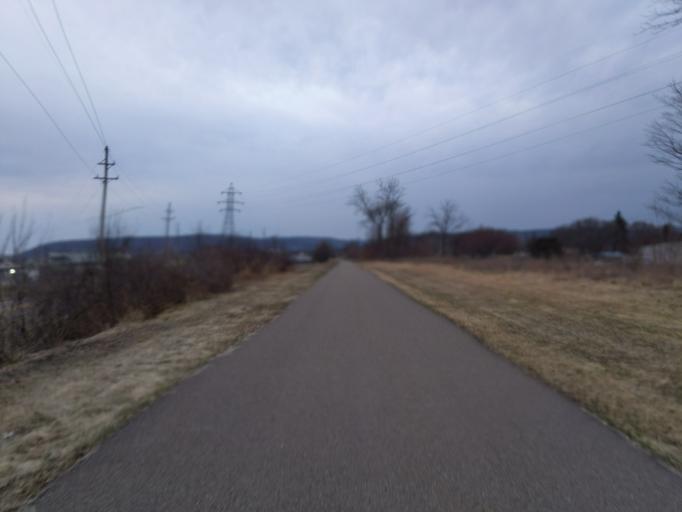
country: US
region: New York
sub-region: Chemung County
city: Elmira
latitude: 42.0980
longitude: -76.7967
